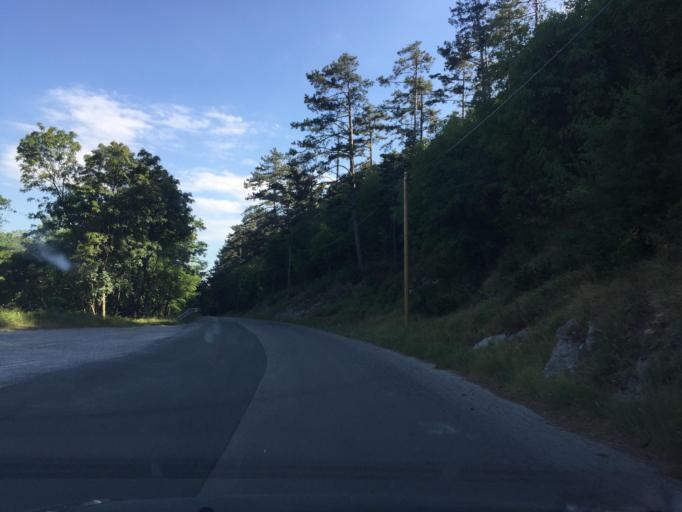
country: HR
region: Primorsko-Goranska
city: Klana
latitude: 45.4571
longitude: 14.3778
